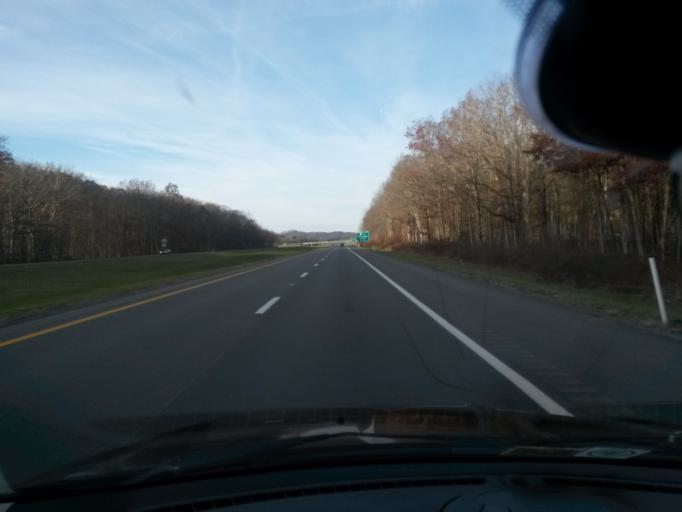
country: US
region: West Virginia
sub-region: Greenbrier County
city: Rainelle
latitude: 37.9069
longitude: -80.6219
